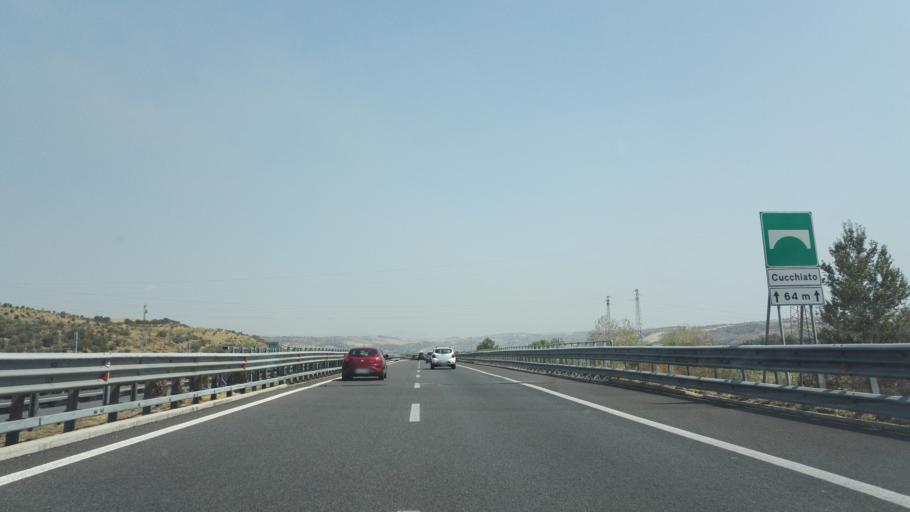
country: IT
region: Calabria
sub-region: Provincia di Cosenza
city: Sartano
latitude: 39.5515
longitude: 16.2304
